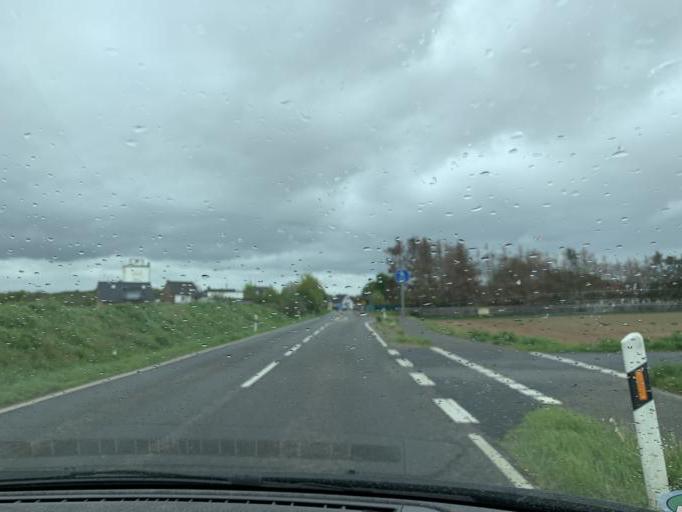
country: DE
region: North Rhine-Westphalia
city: Zulpich
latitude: 50.6646
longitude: 6.6506
